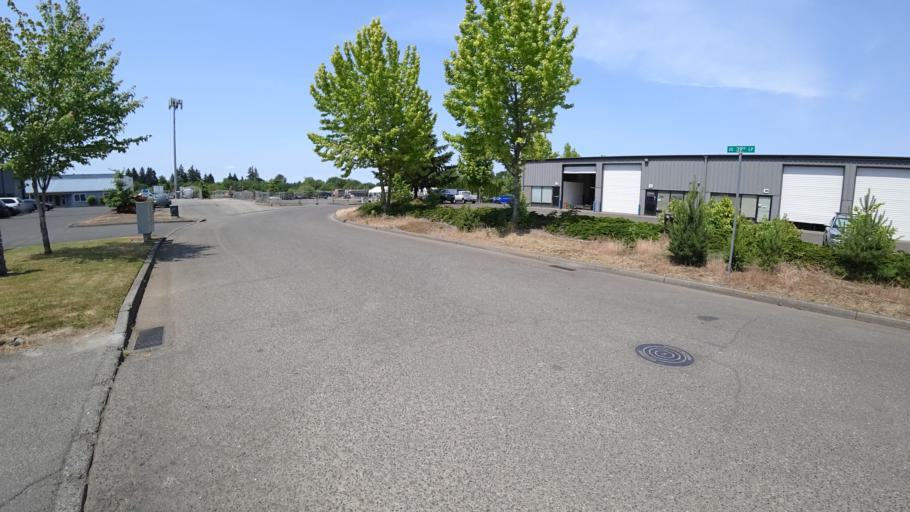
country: US
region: Oregon
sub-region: Washington County
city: Hillsboro
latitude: 45.4992
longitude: -122.9442
